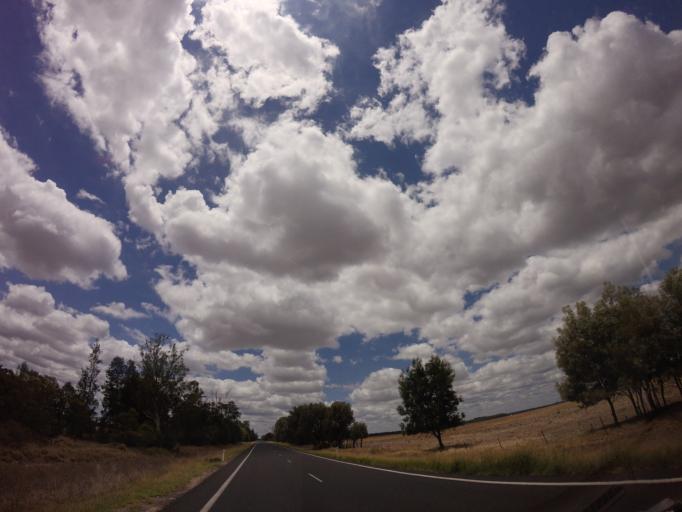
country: AU
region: Queensland
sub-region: Goondiwindi
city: Goondiwindi
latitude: -28.1500
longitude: 150.6825
